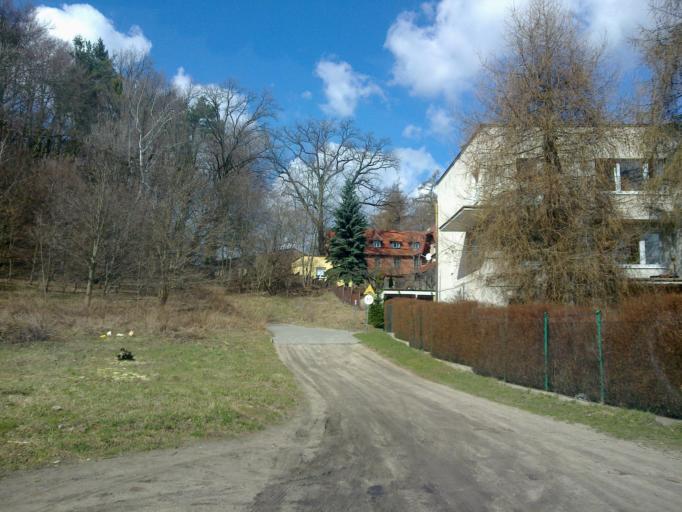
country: PL
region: Pomeranian Voivodeship
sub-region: Sopot
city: Sopot
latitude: 54.3901
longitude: 18.5675
